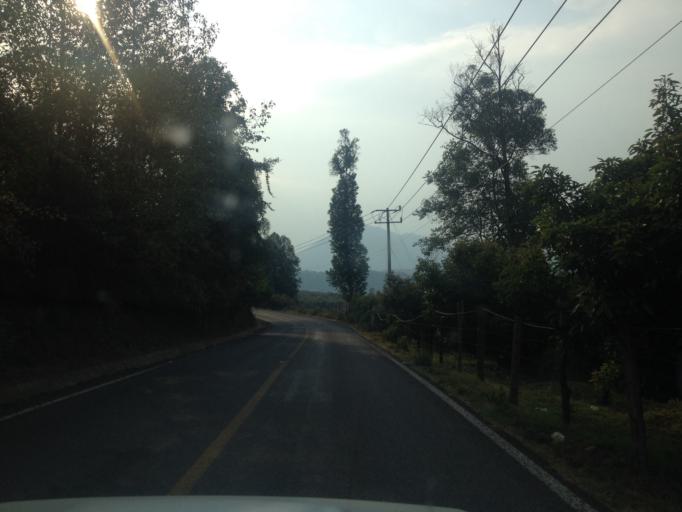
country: MX
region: Michoacan
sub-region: Zitacuaro
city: La Fundicion (Quinta Manzana)
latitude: 19.4878
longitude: -100.3192
